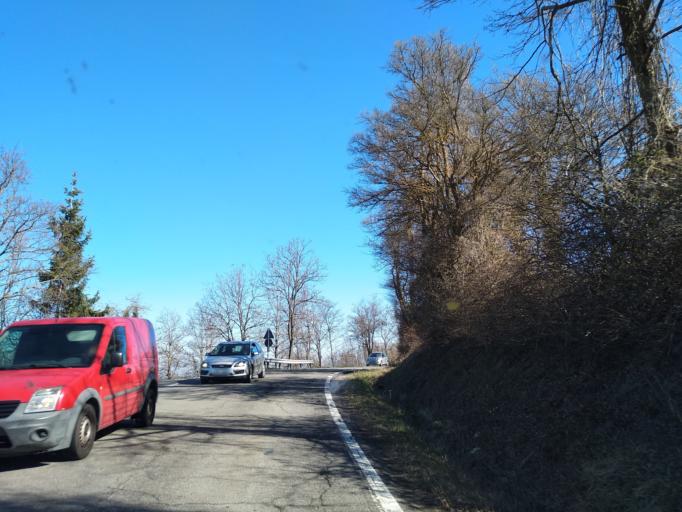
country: IT
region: Emilia-Romagna
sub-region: Provincia di Reggio Emilia
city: Castelnovo ne'Monti
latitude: 44.4207
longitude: 10.4027
